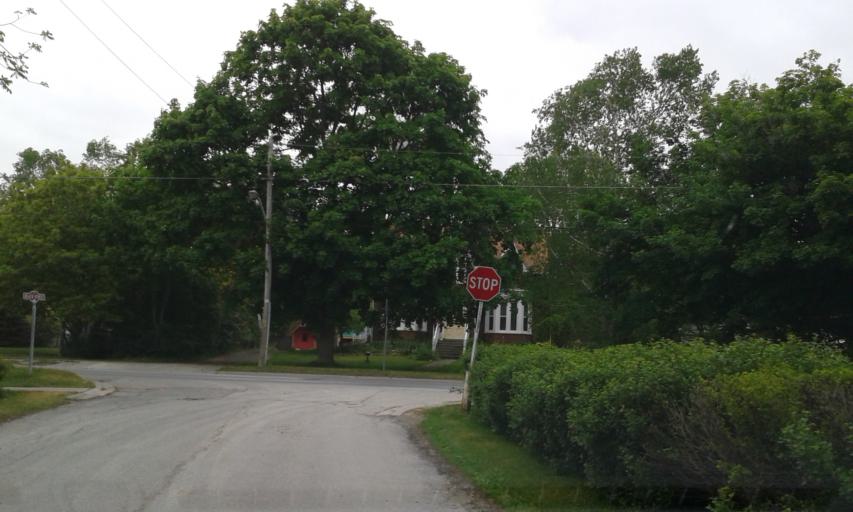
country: CA
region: Ontario
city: Prince Edward
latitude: 43.9516
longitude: -77.3431
